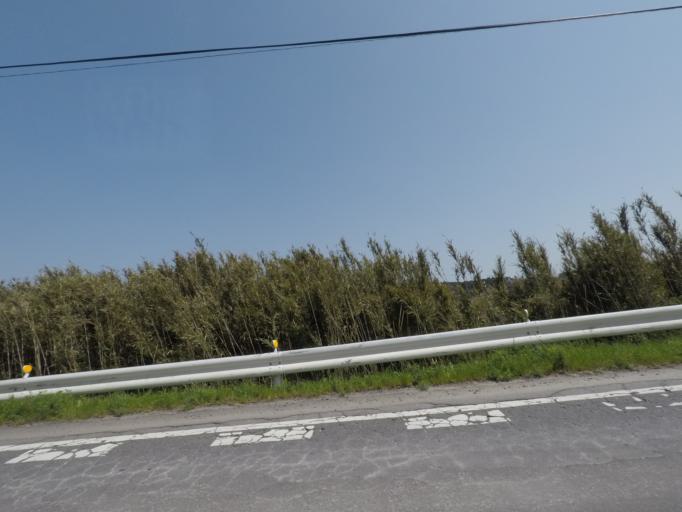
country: JP
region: Chiba
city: Yokaichiba
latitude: 35.6963
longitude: 140.4612
